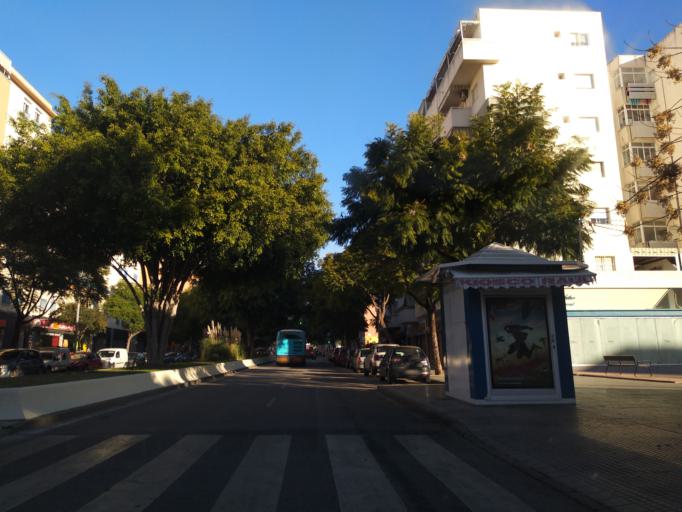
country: ES
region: Andalusia
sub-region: Provincia de Malaga
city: Malaga
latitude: 36.7447
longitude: -4.4264
